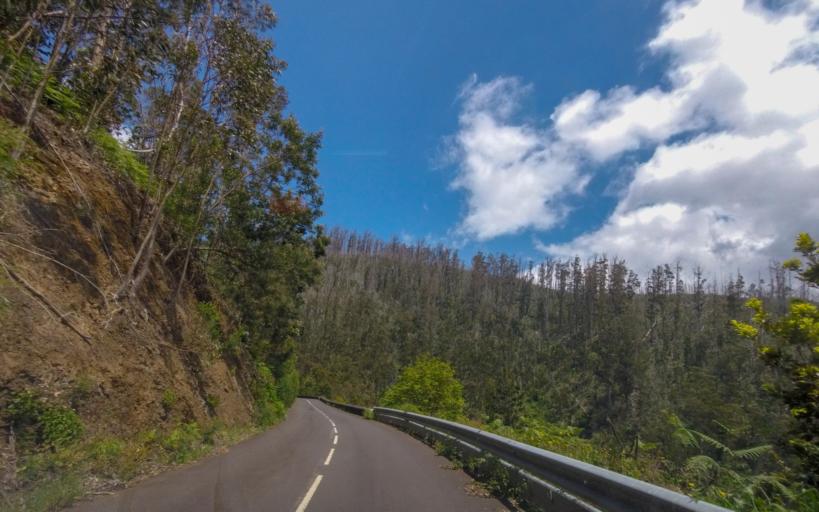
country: PT
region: Madeira
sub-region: Funchal
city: Nossa Senhora do Monte
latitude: 32.6797
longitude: -16.8825
